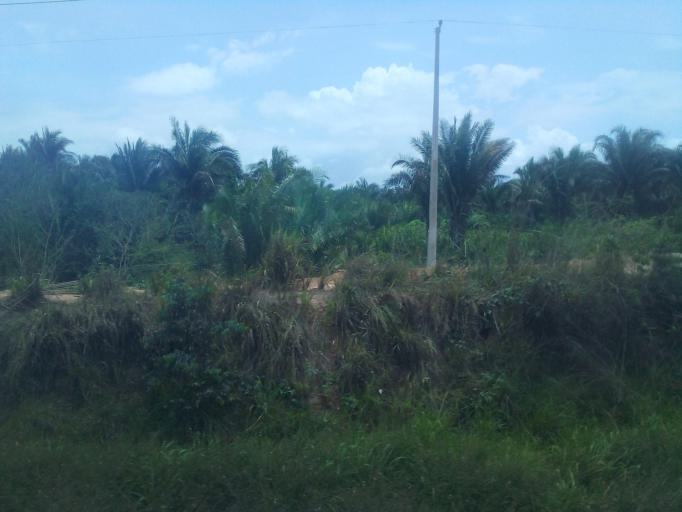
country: BR
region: Maranhao
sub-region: Santa Ines
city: Santa Ines
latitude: -3.7103
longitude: -45.5532
